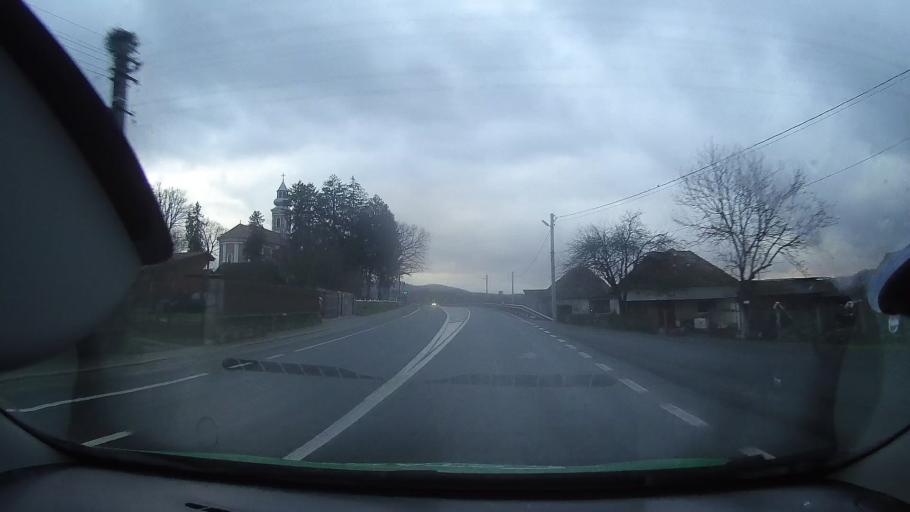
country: RO
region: Hunedoara
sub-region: Comuna Baia de Cris
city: Baia de Cris
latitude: 46.1686
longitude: 22.7342
